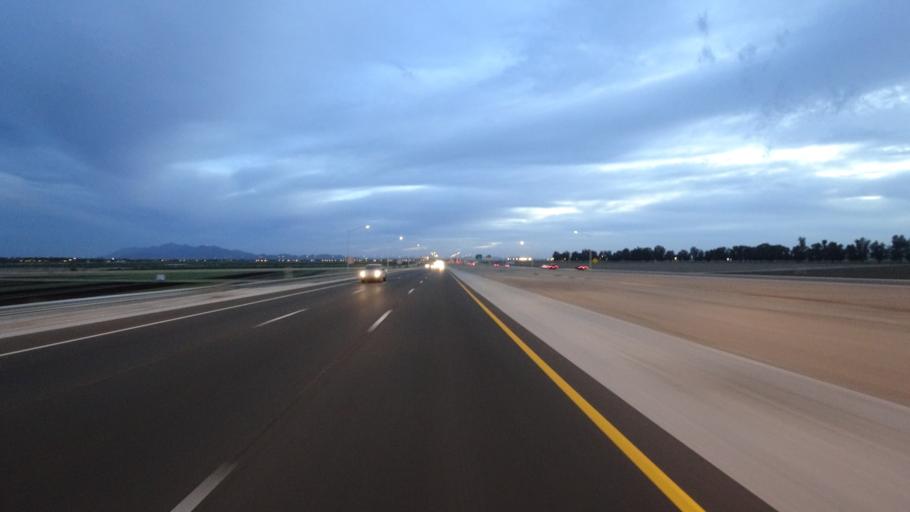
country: US
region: Arizona
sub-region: Maricopa County
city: Citrus Park
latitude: 33.4913
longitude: -112.4209
